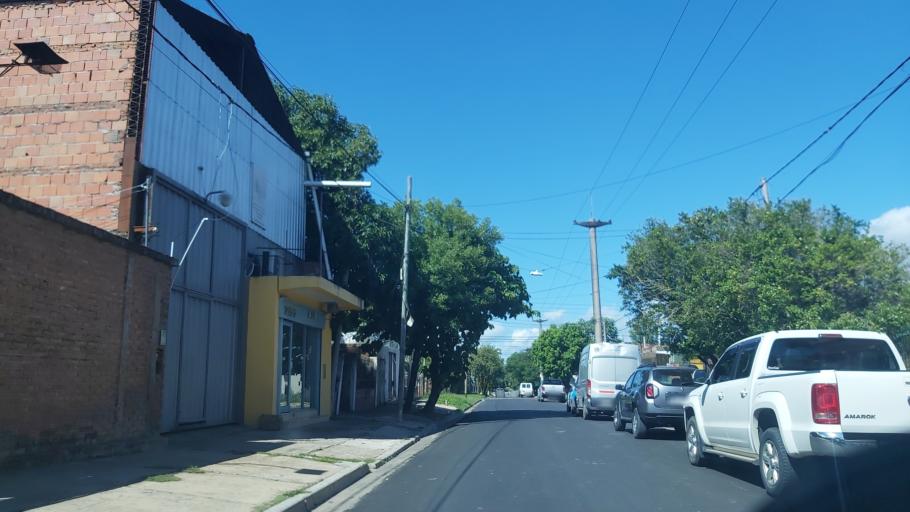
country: AR
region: Corrientes
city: Corrientes
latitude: -27.4809
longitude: -58.8478
